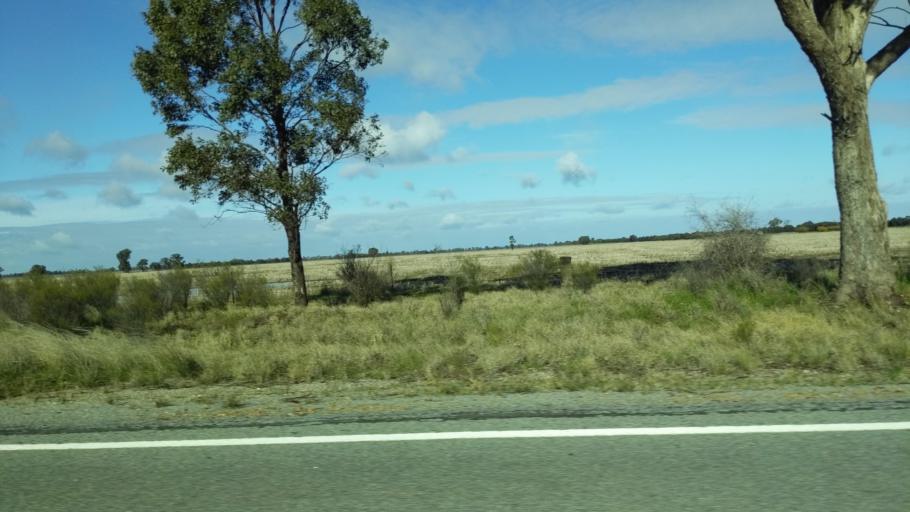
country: AU
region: New South Wales
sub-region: Narrandera
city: Narrandera
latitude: -34.7571
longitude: 146.8677
